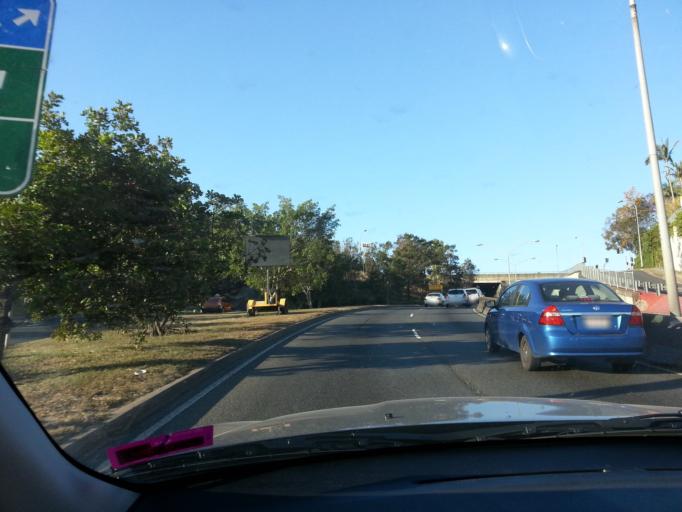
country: AU
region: Queensland
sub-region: Brisbane
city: Spring Hill
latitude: -27.4596
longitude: 153.0117
